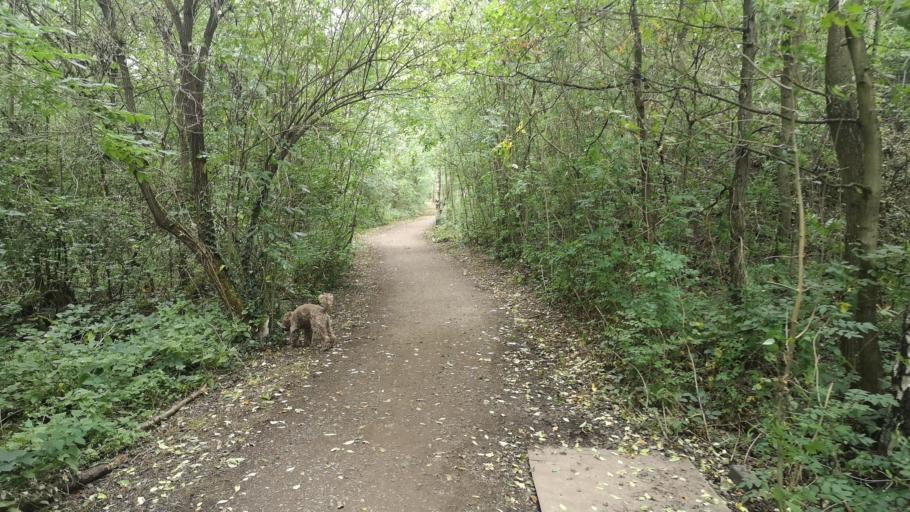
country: GB
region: England
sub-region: Barnsley
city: Royston
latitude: 53.6156
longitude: -1.4499
